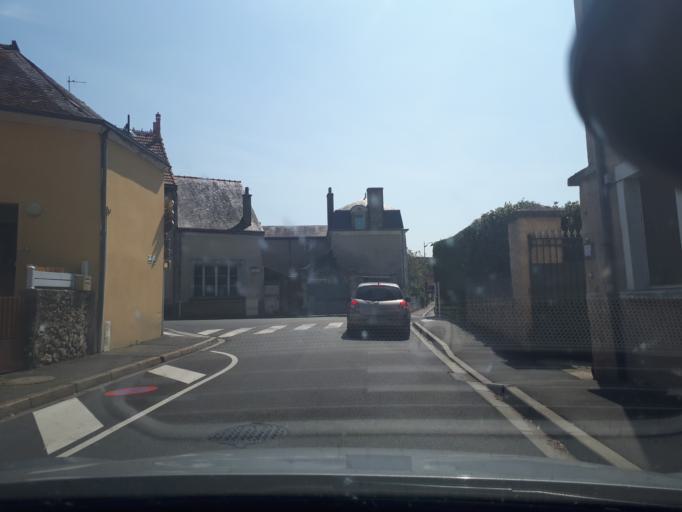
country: FR
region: Pays de la Loire
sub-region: Departement de la Sarthe
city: Le Breil-sur-Merize
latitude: 48.0088
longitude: 0.4771
